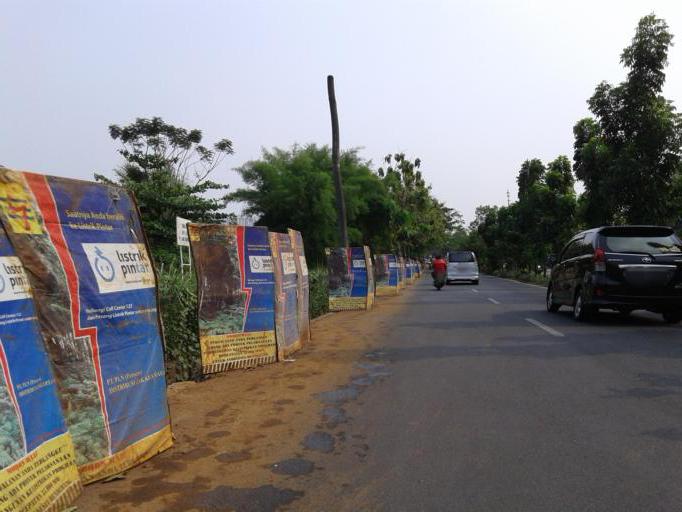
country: ID
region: West Java
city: Pamulang
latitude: -6.3073
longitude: 106.7816
